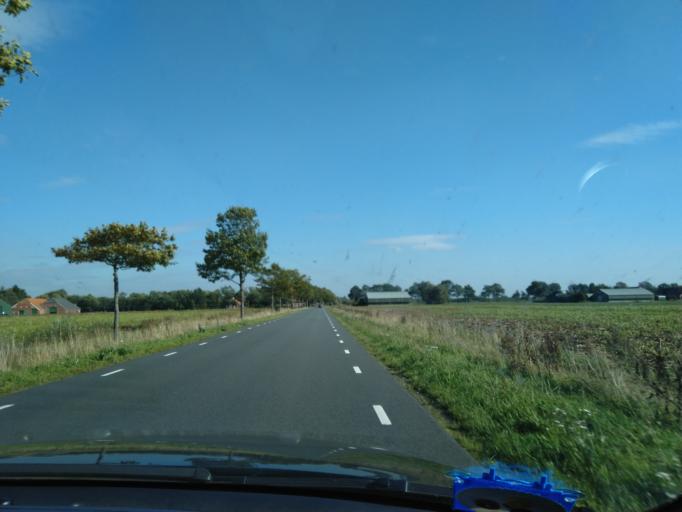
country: NL
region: Groningen
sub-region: Gemeente Veendam
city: Veendam
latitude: 53.0915
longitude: 6.8283
